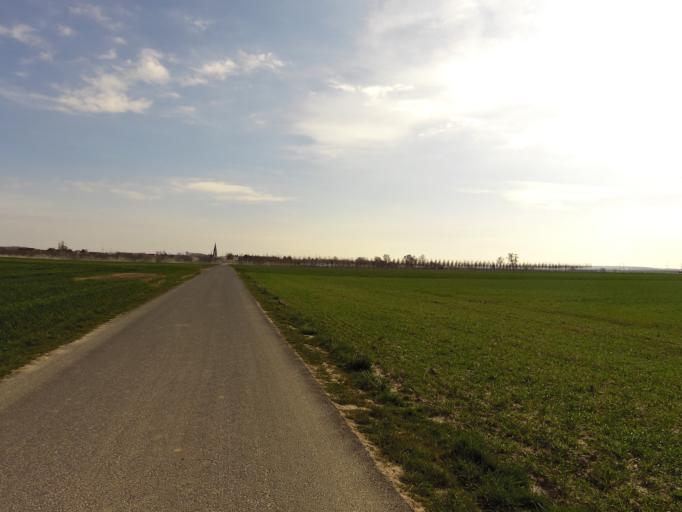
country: DE
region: North Rhine-Westphalia
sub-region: Regierungsbezirk Koln
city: Rheinbach
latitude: 50.6448
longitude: 6.9718
